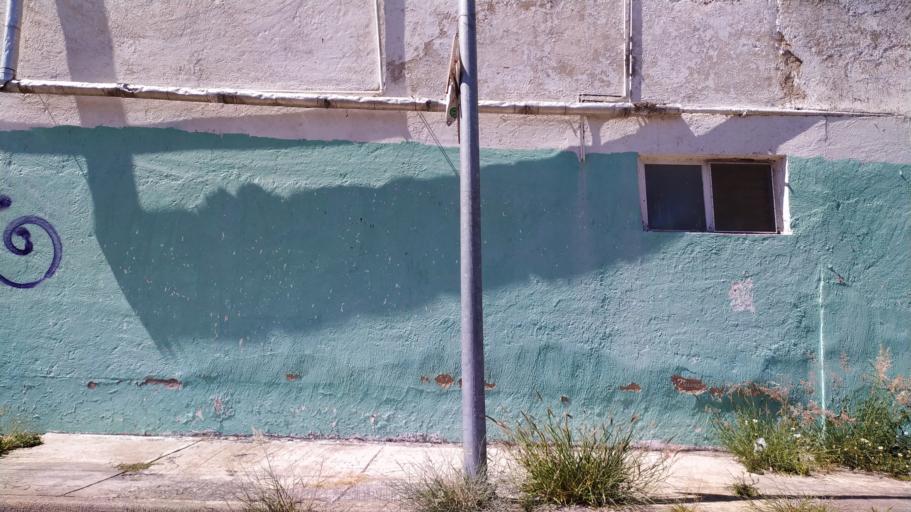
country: MX
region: Jalisco
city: Guadalajara
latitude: 20.6738
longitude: -103.3973
